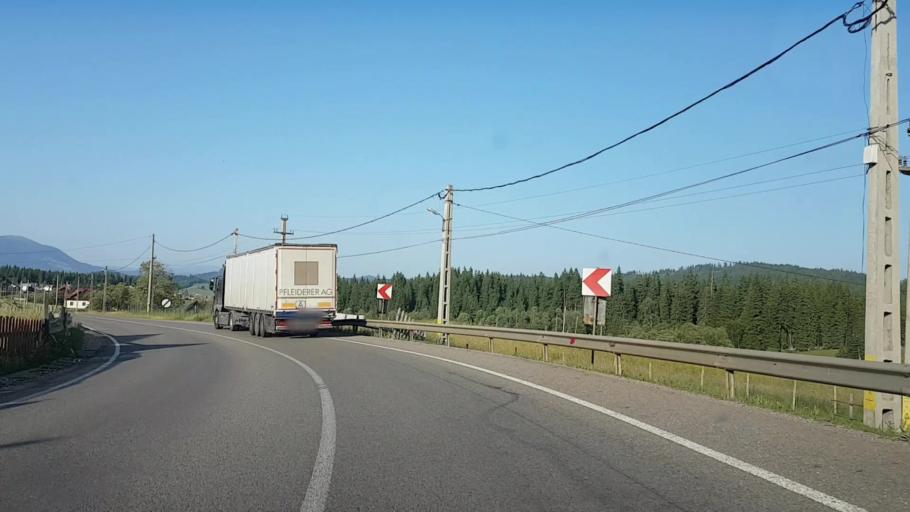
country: RO
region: Suceava
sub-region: Comuna Poiana Stampei
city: Poiana Stampei
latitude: 47.3008
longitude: 25.1054
